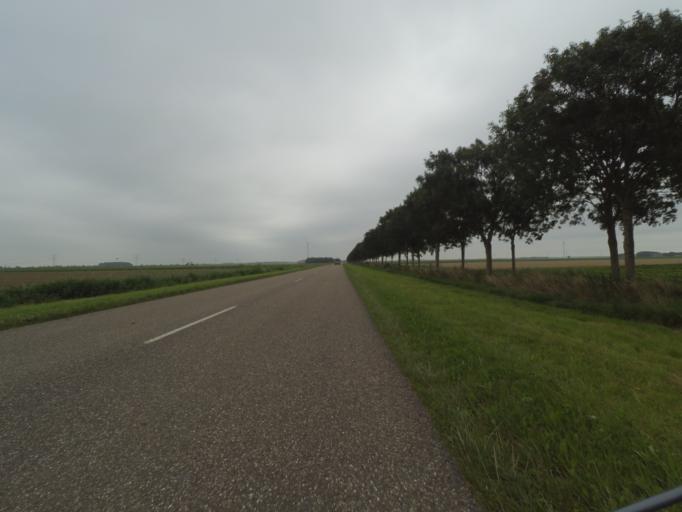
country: NL
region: Flevoland
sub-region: Gemeente Lelystad
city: Lelystad
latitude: 52.4053
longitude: 5.3753
